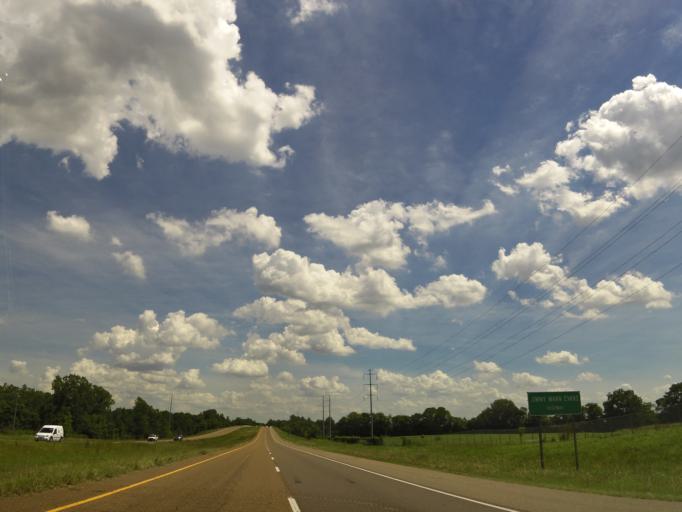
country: US
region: Tennessee
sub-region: Dyer County
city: Dyersburg
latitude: 36.0578
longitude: -89.3388
